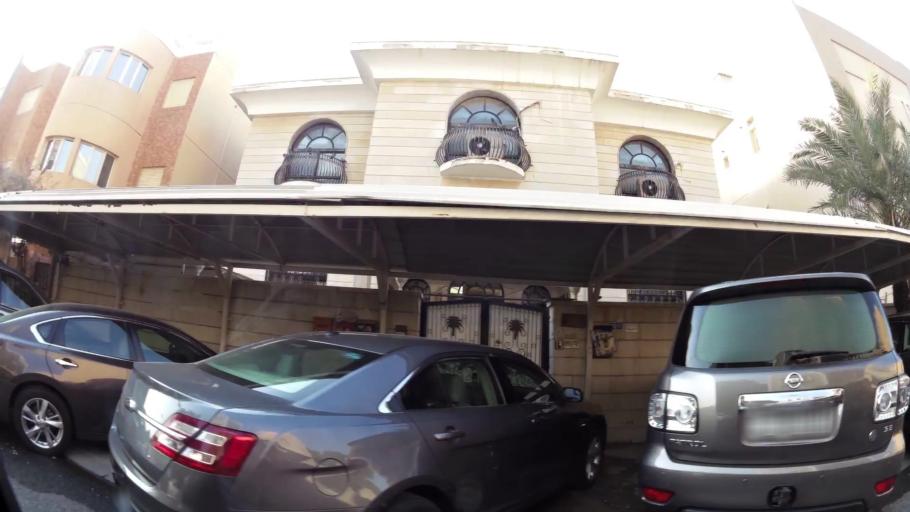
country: KW
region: Al Asimah
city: Ad Dasmah
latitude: 29.3628
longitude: 47.9993
